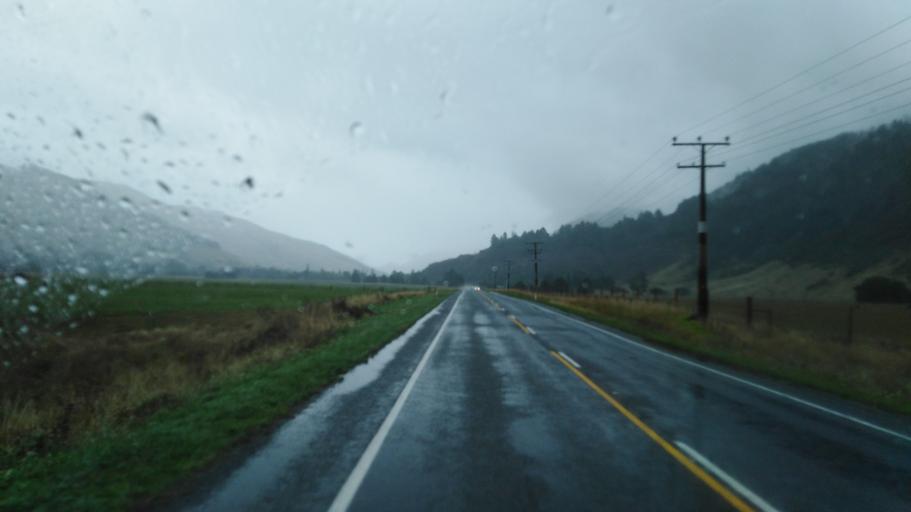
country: NZ
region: Marlborough
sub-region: Marlborough District
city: Picton
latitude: -41.3213
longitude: 173.7643
